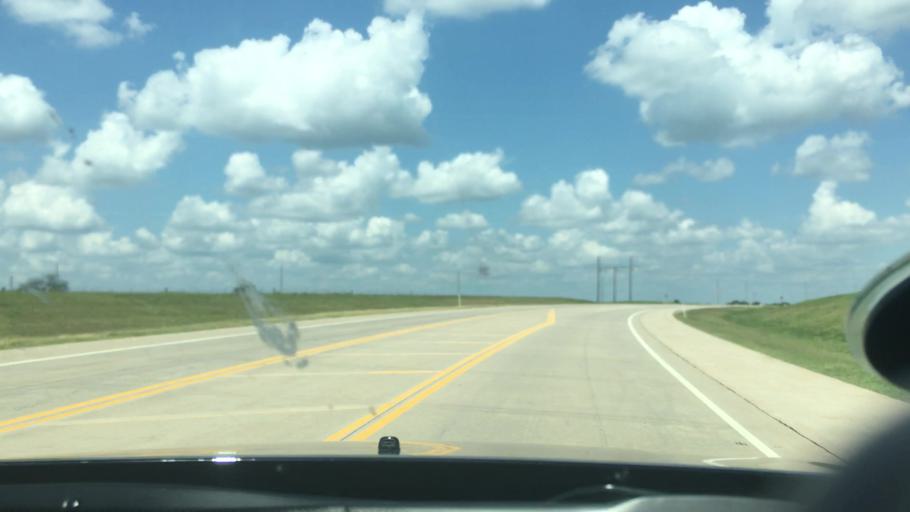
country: US
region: Oklahoma
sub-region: Garvin County
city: Stratford
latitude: 34.6492
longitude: -96.8382
